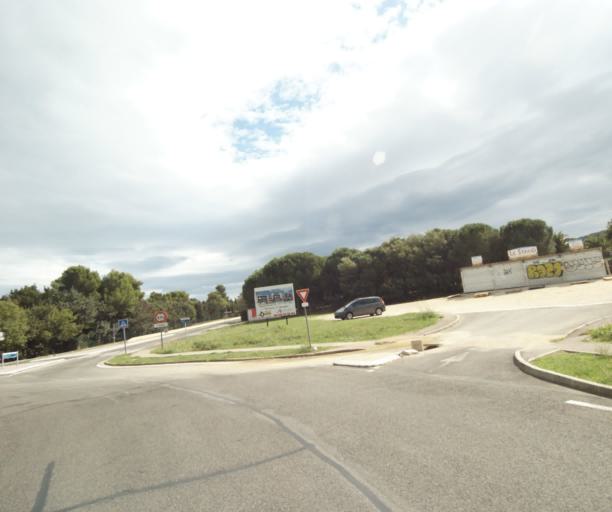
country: FR
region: Languedoc-Roussillon
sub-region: Departement des Pyrenees-Orientales
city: Argelers
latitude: 42.5397
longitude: 3.0365
